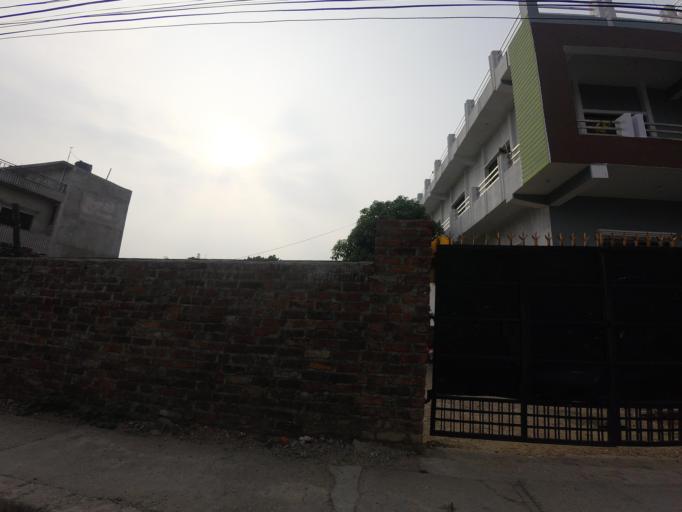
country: NP
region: Western Region
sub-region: Lumbini Zone
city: Bhairahawa
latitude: 27.4940
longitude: 83.4486
